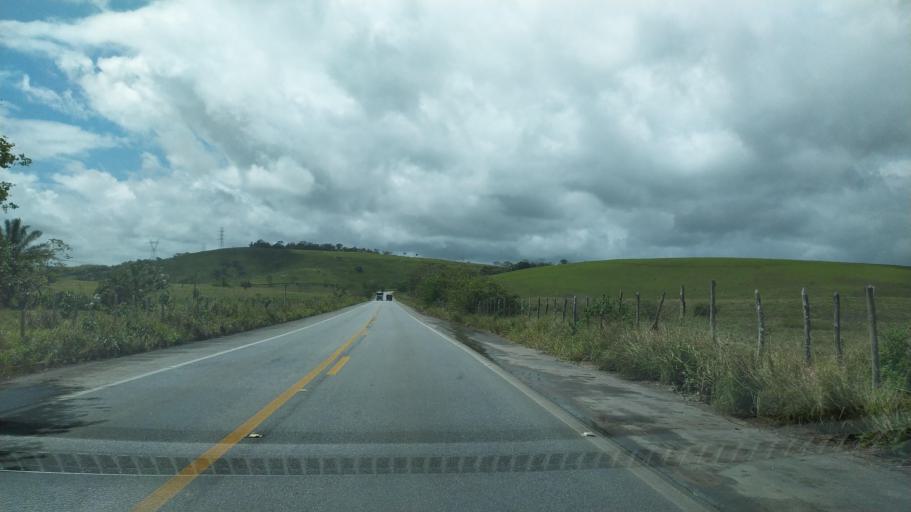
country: BR
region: Alagoas
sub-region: Messias
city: Messias
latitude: -9.3457
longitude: -35.8826
